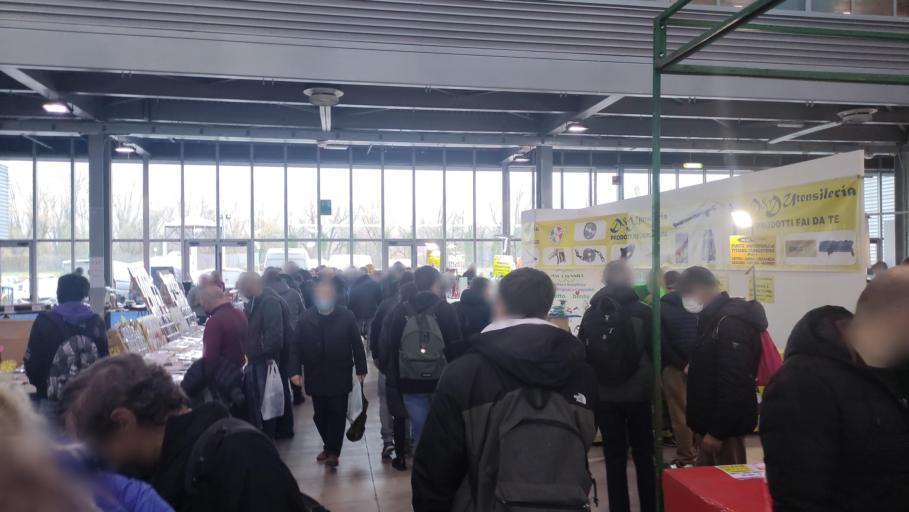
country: IT
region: Friuli Venezia Giulia
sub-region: Provincia di Pordenone
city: Pordenone
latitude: 45.9489
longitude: 12.6560
